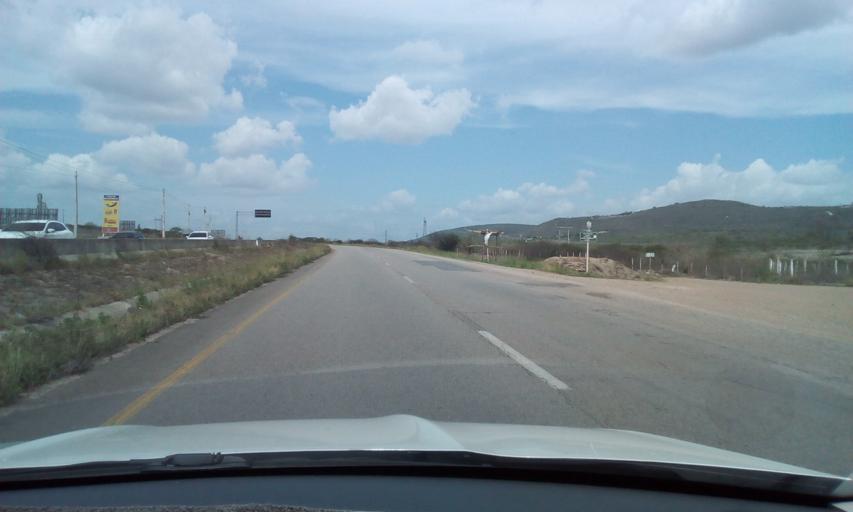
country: BR
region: Pernambuco
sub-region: Bezerros
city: Bezerros
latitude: -8.2350
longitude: -35.7202
